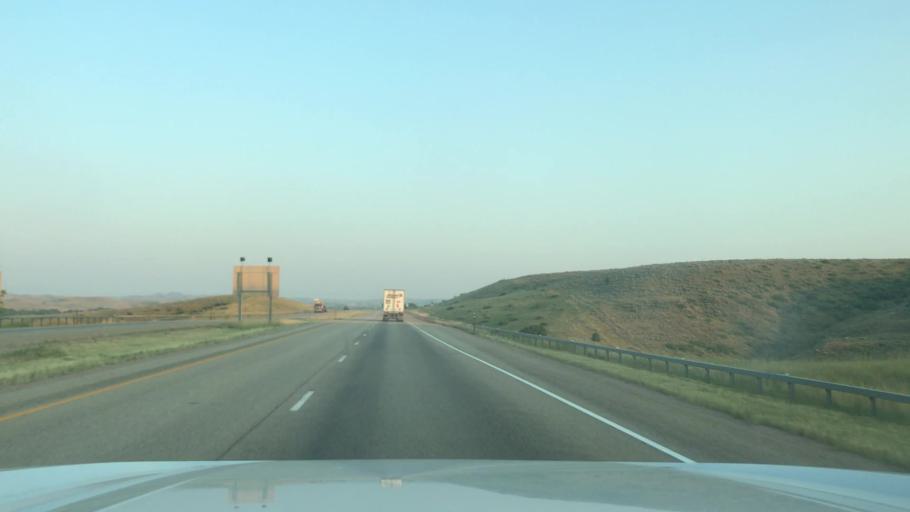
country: US
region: Wyoming
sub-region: Sheridan County
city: Sheridan
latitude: 44.8776
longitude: -106.9999
